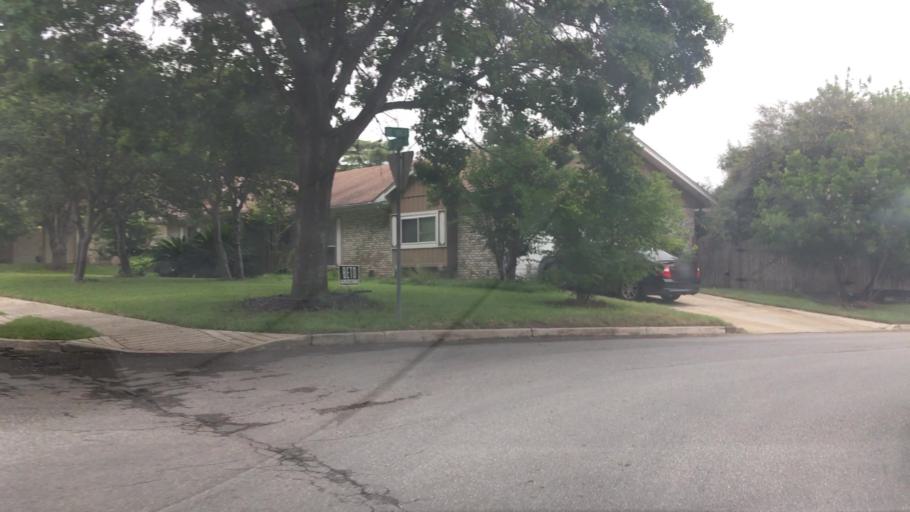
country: US
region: Texas
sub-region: Bexar County
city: Universal City
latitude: 29.5516
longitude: -98.3148
